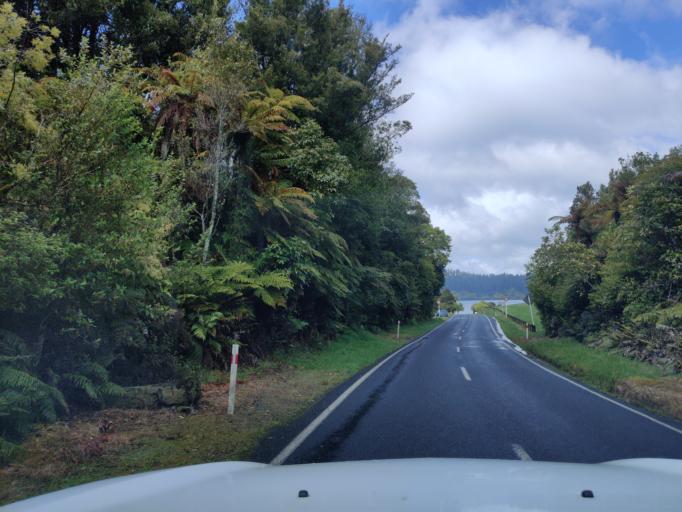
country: NZ
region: Bay of Plenty
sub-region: Rotorua District
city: Rotorua
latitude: -38.1835
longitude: 176.3281
